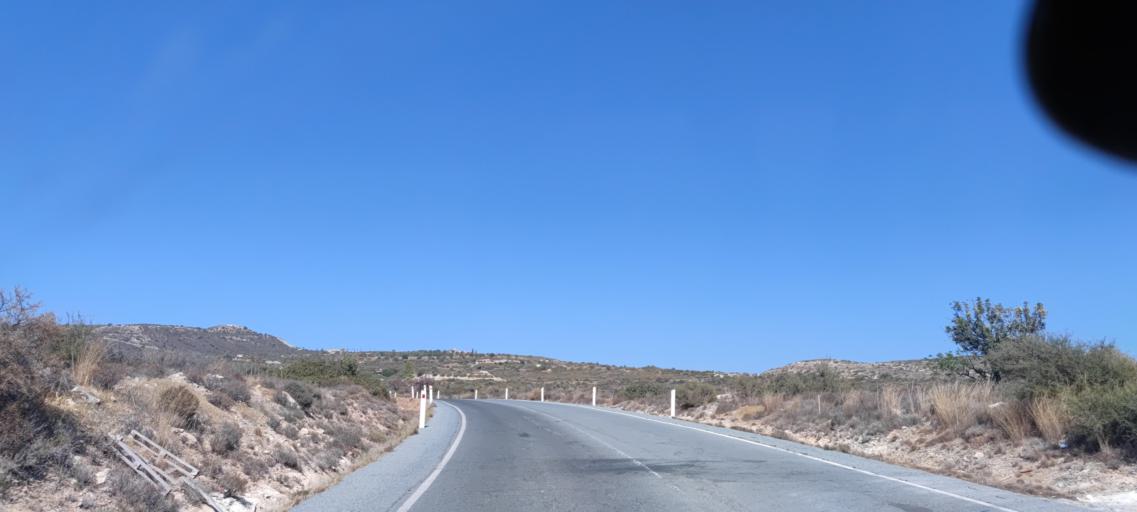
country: CY
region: Limassol
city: Mouttagiaka
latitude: 34.7368
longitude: 33.0645
